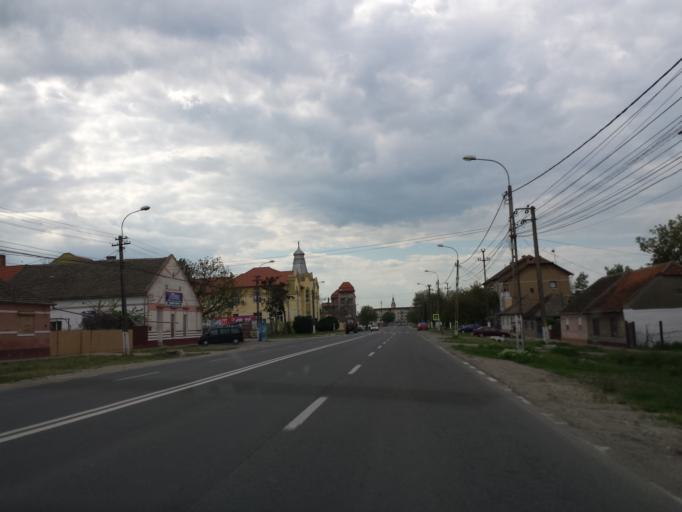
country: RO
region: Timis
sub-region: Oras Sannicolau Mare
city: Sannicolau Mare
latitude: 46.0679
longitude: 20.6380
